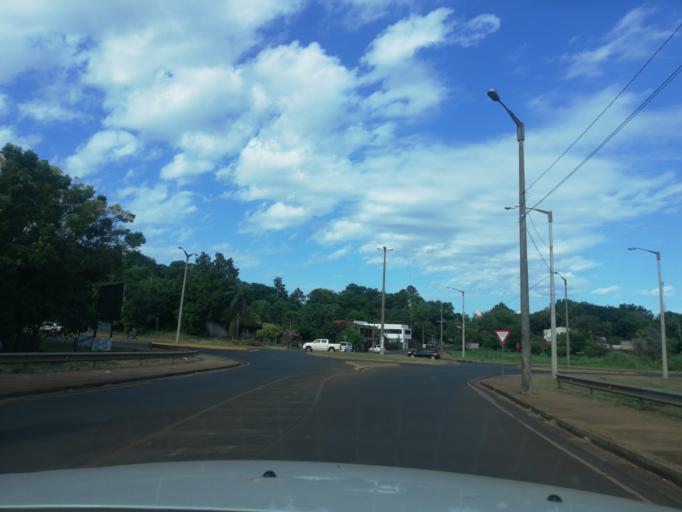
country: PY
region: Itapua
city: Encarnacion
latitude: -27.3435
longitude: -55.8528
